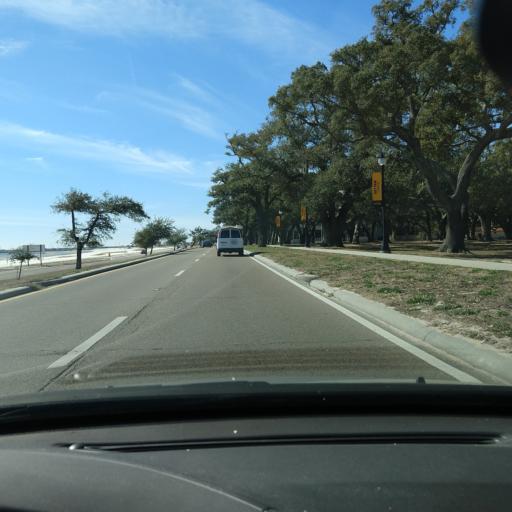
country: US
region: Mississippi
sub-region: Harrison County
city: Long Beach
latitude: 30.3511
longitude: -89.1352
